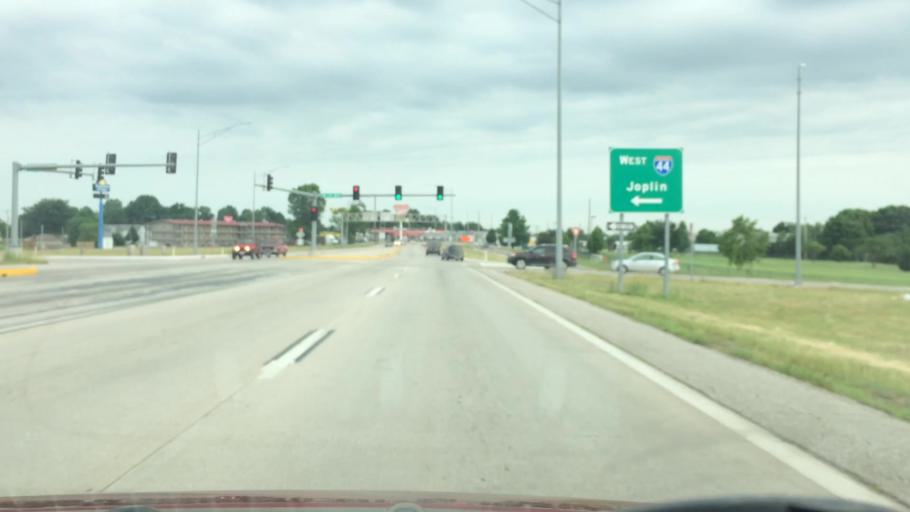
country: US
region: Missouri
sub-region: Greene County
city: Springfield
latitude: 37.2512
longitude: -93.2630
